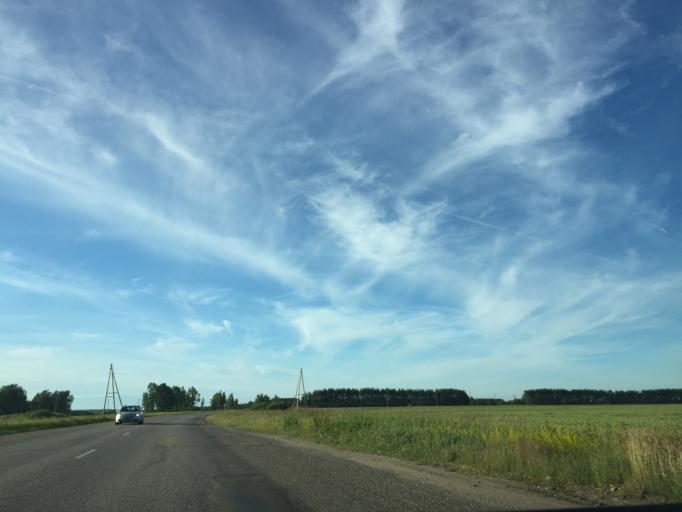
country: LV
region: Ventspils
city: Ventspils
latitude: 57.3323
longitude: 21.5639
